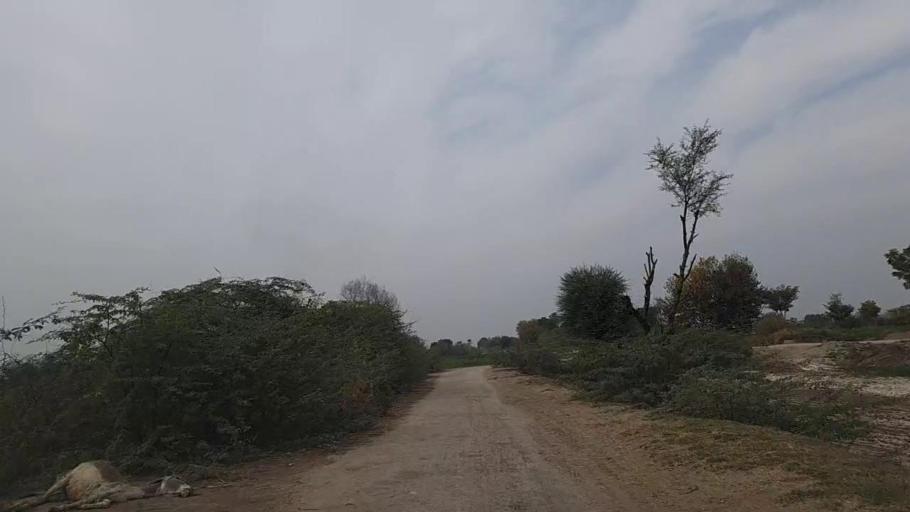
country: PK
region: Sindh
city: Daur
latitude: 26.4446
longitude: 68.4555
